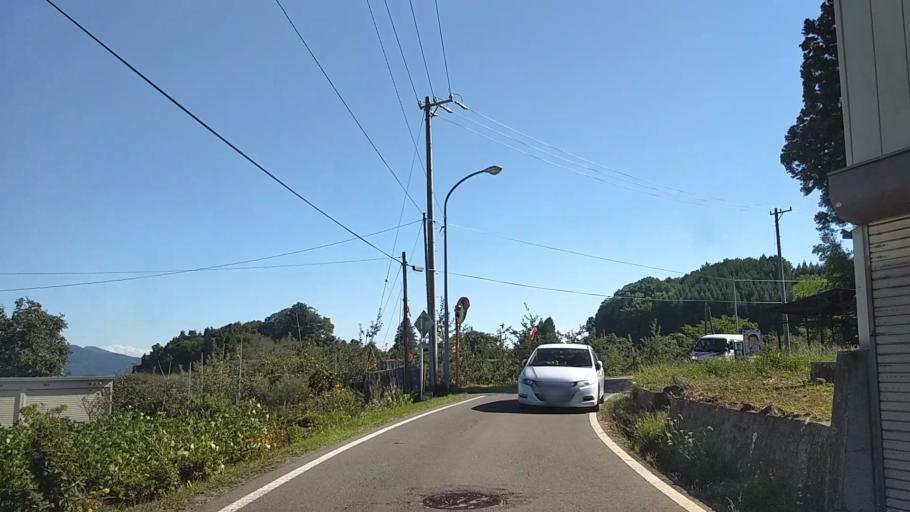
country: JP
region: Nagano
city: Nagano-shi
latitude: 36.5843
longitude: 138.1037
